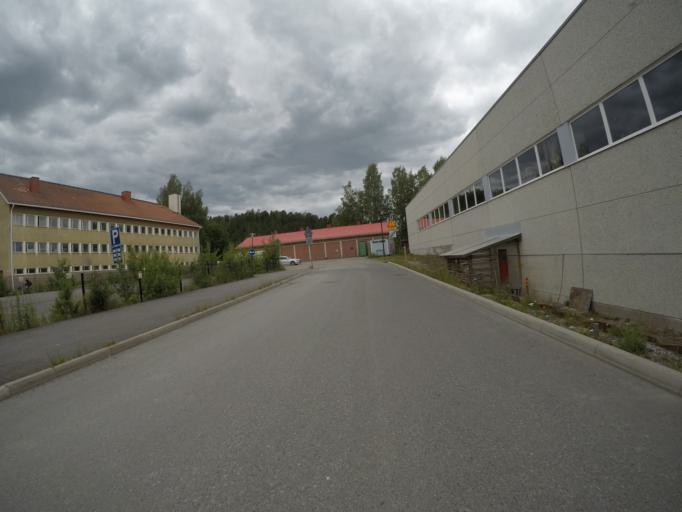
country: FI
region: Haeme
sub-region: Haemeenlinna
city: Haemeenlinna
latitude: 60.9928
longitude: 24.4349
